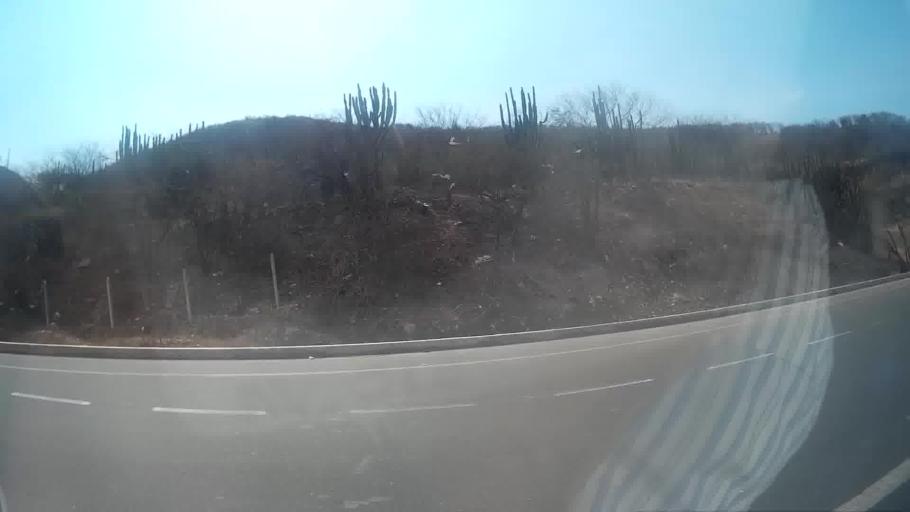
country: CO
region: Magdalena
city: Santa Marta
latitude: 11.1802
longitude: -74.2277
